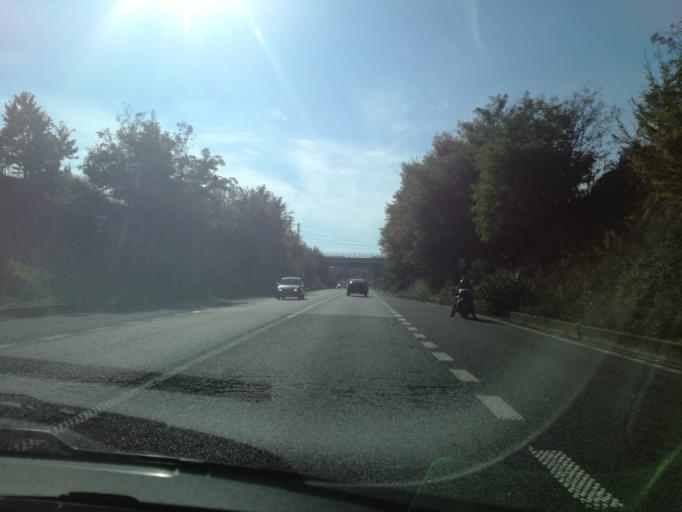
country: IT
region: Lombardy
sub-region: Provincia di Bergamo
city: Mapello
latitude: 45.7077
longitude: 9.5631
